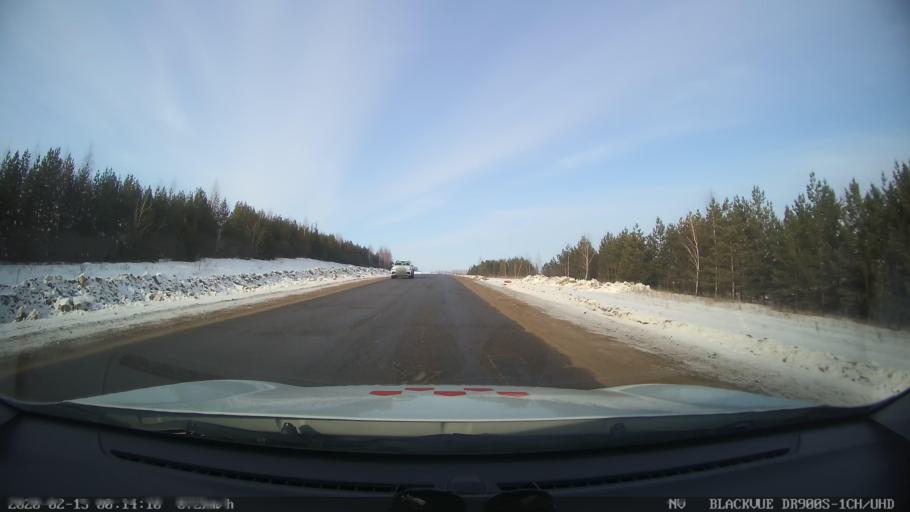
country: RU
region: Tatarstan
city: Stolbishchi
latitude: 55.4832
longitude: 49.0044
